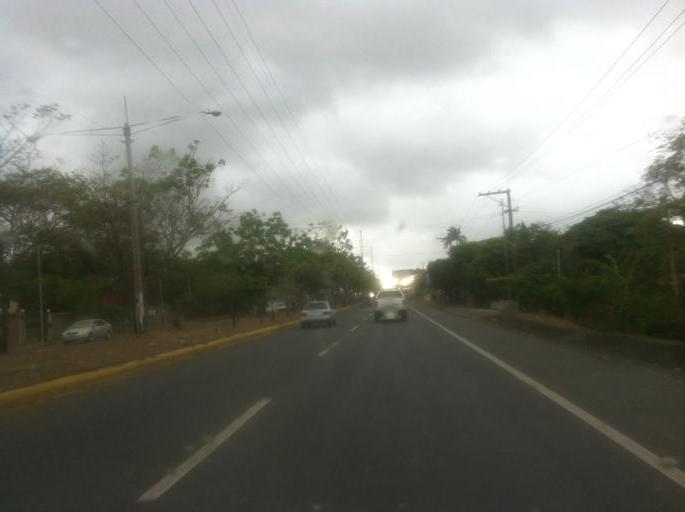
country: NI
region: Managua
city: Managua
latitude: 12.0835
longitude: -86.2281
